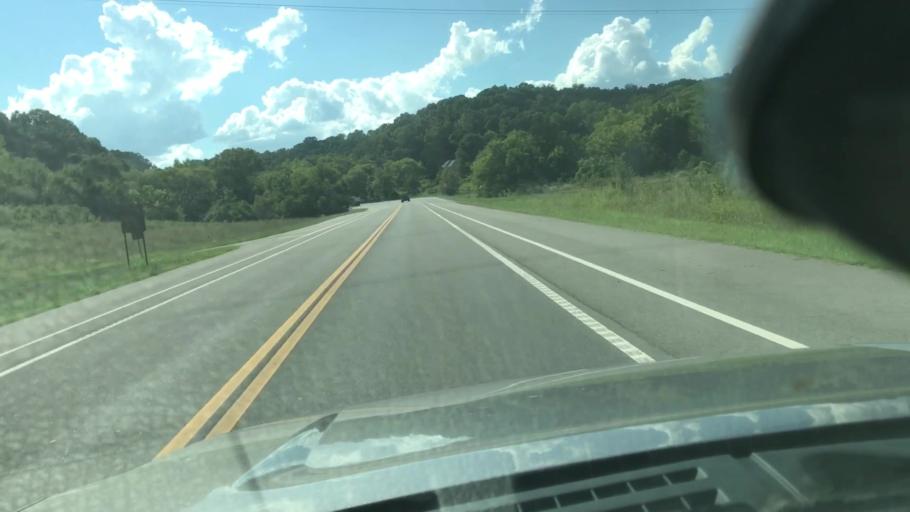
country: US
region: Tennessee
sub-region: Cheatham County
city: Pegram
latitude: 36.0347
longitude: -86.9777
